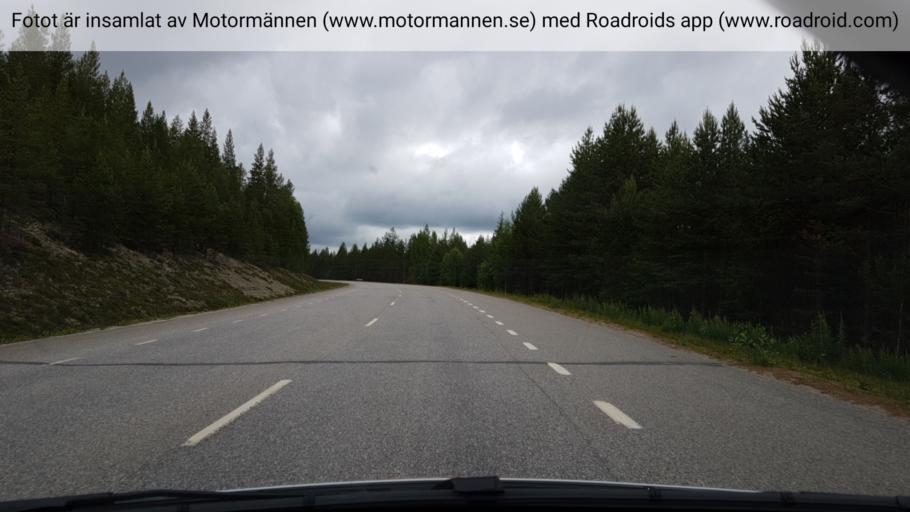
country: SE
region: Vaesterbotten
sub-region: Norsjo Kommun
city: Norsjoe
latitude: 64.5893
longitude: 19.2964
